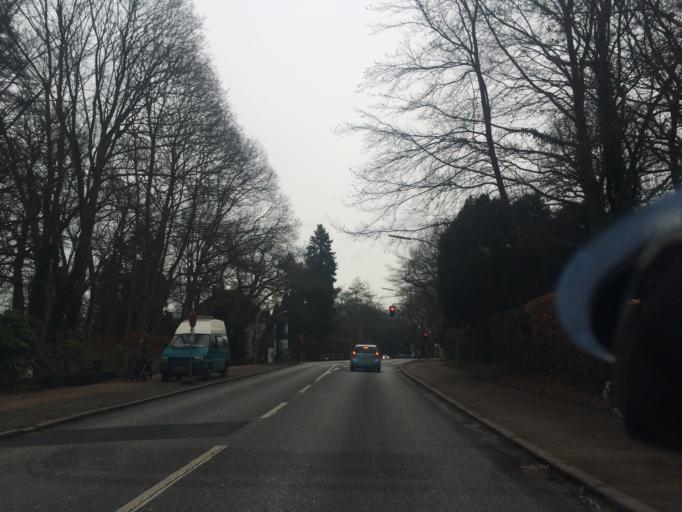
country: DE
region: Hamburg
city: Altona
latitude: 53.5467
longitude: 9.8787
